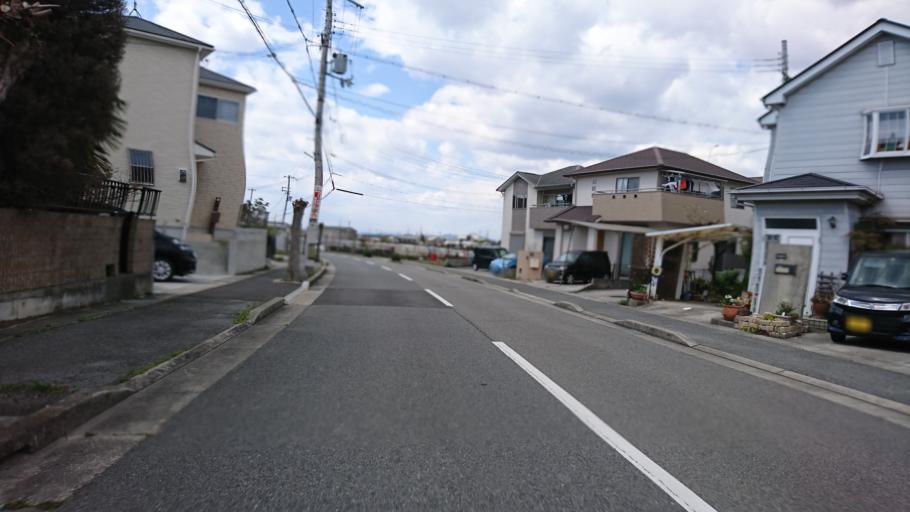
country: JP
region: Hyogo
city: Miki
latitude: 34.7513
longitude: 134.9156
